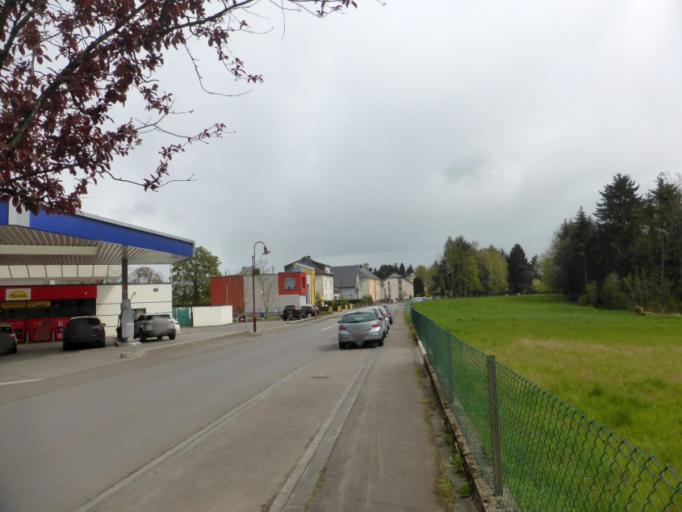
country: LU
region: Luxembourg
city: Bridel
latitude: 49.6571
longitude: 6.0825
